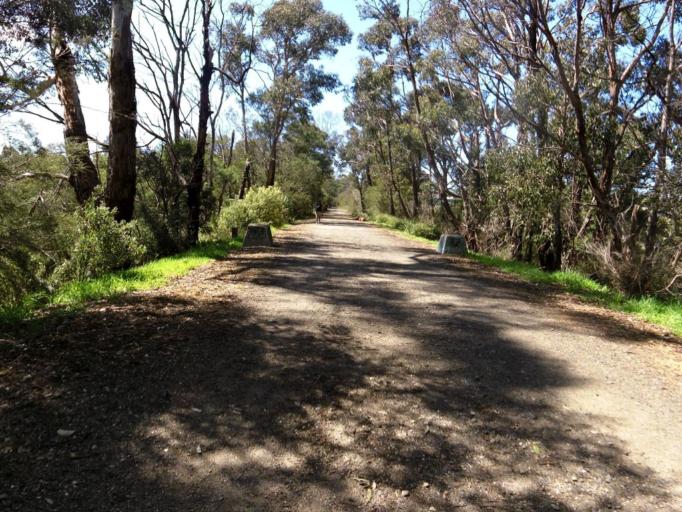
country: AU
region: Victoria
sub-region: Latrobe
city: Moe
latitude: -38.1754
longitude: 146.2743
